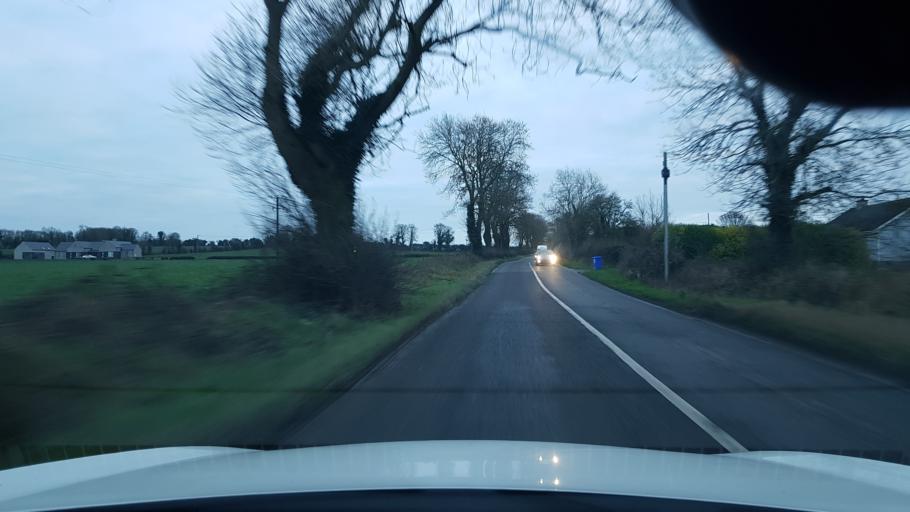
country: IE
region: Leinster
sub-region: An Mhi
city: Navan
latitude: 53.6936
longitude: -6.6755
